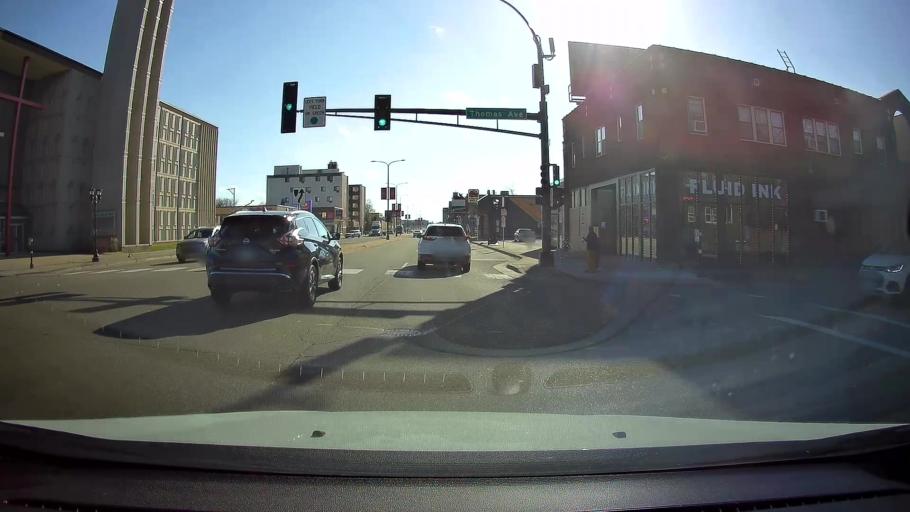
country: US
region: Minnesota
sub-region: Ramsey County
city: Falcon Heights
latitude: 44.9594
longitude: -93.1671
